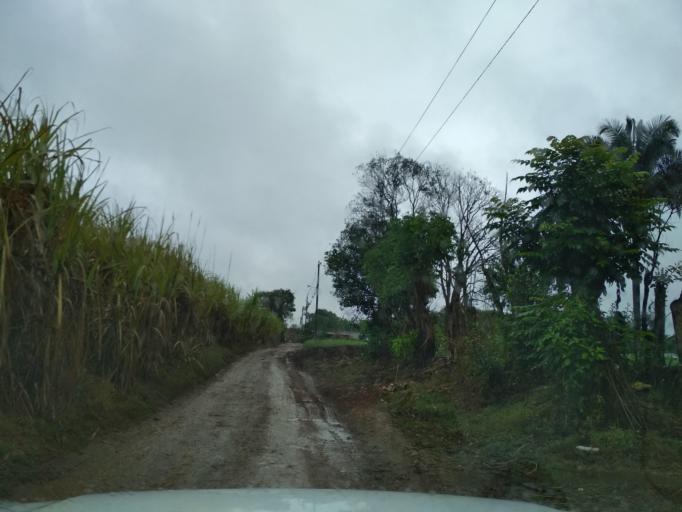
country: MX
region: Veracruz
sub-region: Amatlan de los Reyes
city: Centro de Readaptacion Social
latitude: 18.8333
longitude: -96.9316
